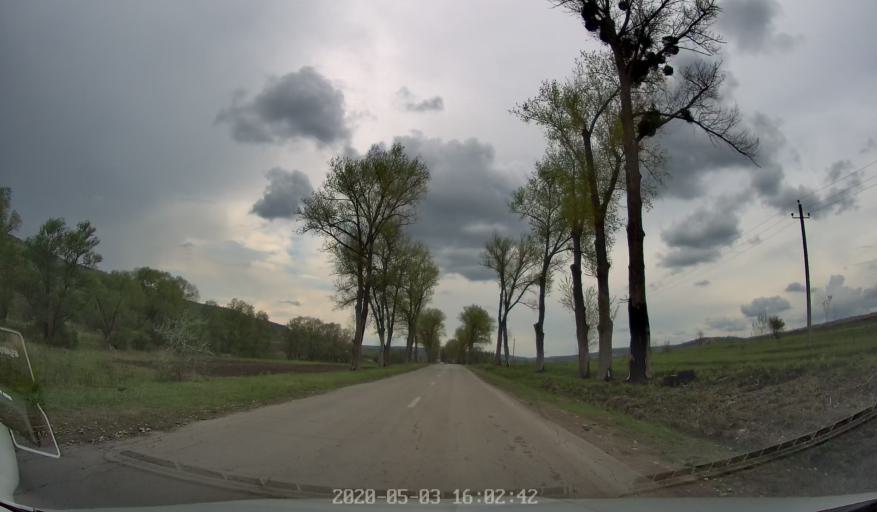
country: MD
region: Stinga Nistrului
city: Bucovat
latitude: 47.1748
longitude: 28.3918
